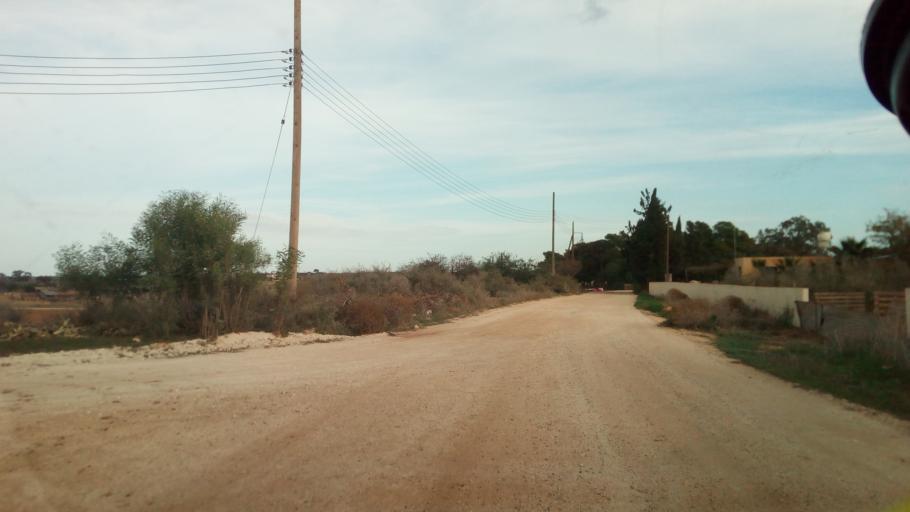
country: CY
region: Ammochostos
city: Avgorou
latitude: 35.0572
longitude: 33.8773
